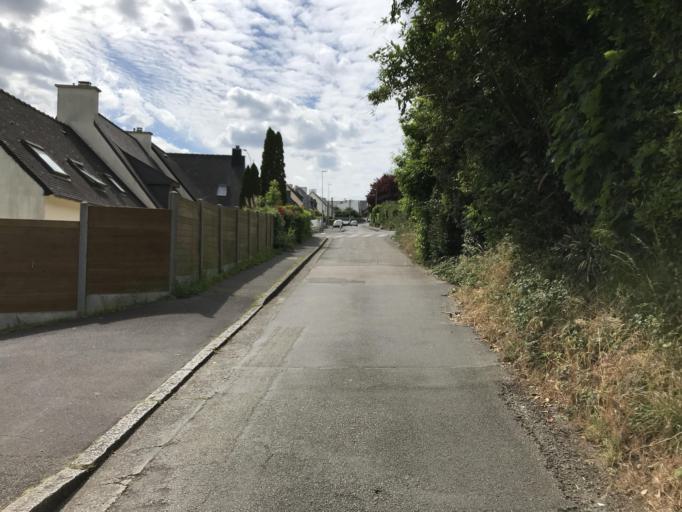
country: FR
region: Brittany
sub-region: Departement du Finistere
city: Brest
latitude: 48.3964
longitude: -4.4436
